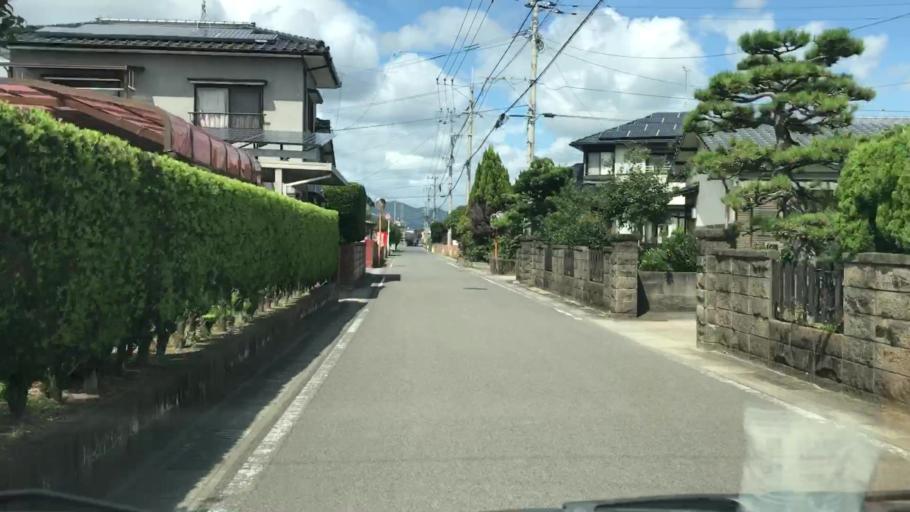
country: JP
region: Saga Prefecture
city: Saga-shi
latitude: 33.2416
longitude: 130.2016
